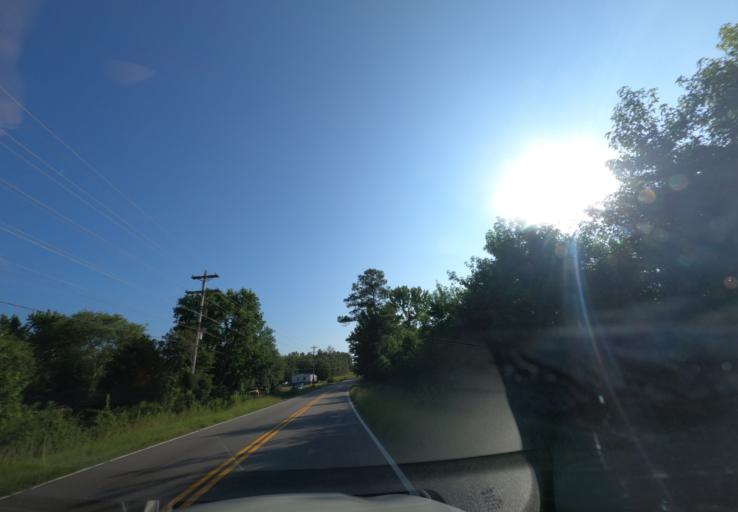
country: US
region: South Carolina
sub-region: Edgefield County
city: Murphys Estates
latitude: 33.5781
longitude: -81.9912
